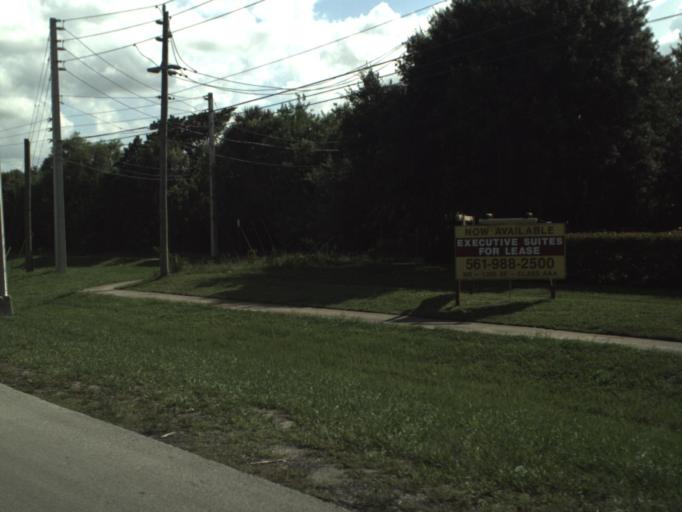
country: US
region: Florida
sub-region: Palm Beach County
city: Boca Pointe
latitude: 26.3738
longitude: -80.2037
